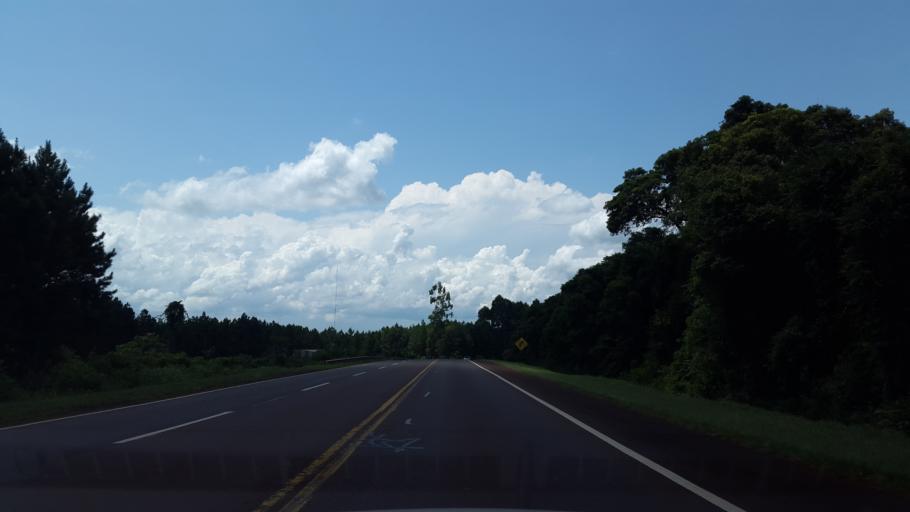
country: AR
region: Misiones
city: El Alcazar
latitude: -26.6950
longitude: -54.8331
